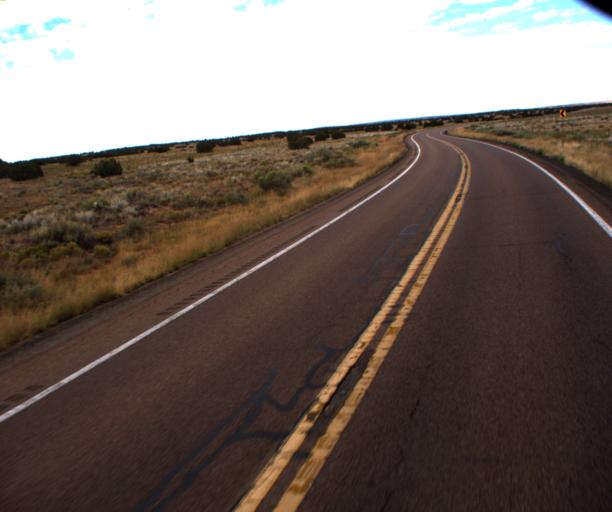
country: US
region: Arizona
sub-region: Navajo County
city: Heber-Overgaard
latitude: 34.5576
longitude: -110.4133
